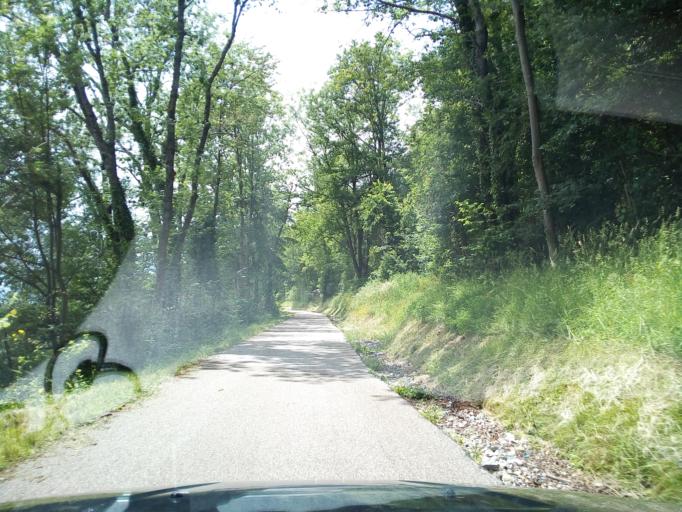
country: FR
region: Rhone-Alpes
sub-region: Departement de l'Isere
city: Herbeys
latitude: 45.1517
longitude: 5.7882
